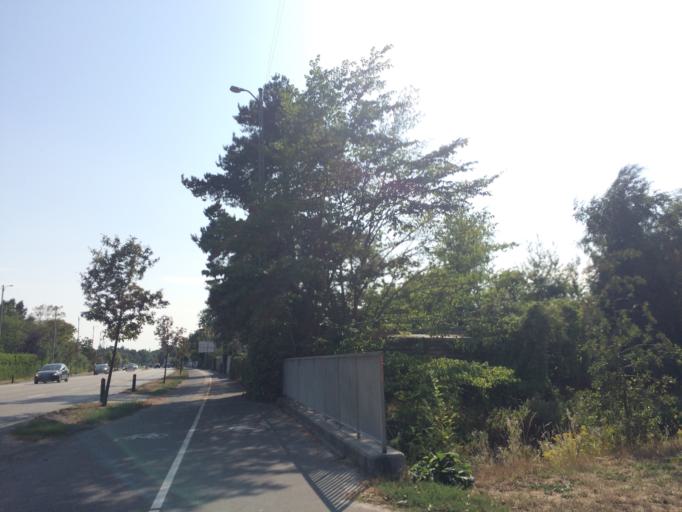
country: DK
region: Capital Region
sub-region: Ishoj Kommune
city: Ishoj
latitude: 55.6029
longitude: 12.3520
